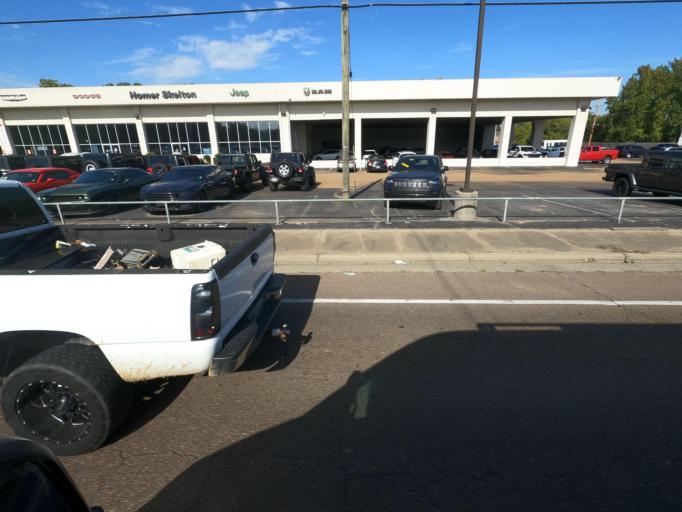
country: US
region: Tennessee
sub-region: Shelby County
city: Millington
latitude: 35.3358
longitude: -89.9163
